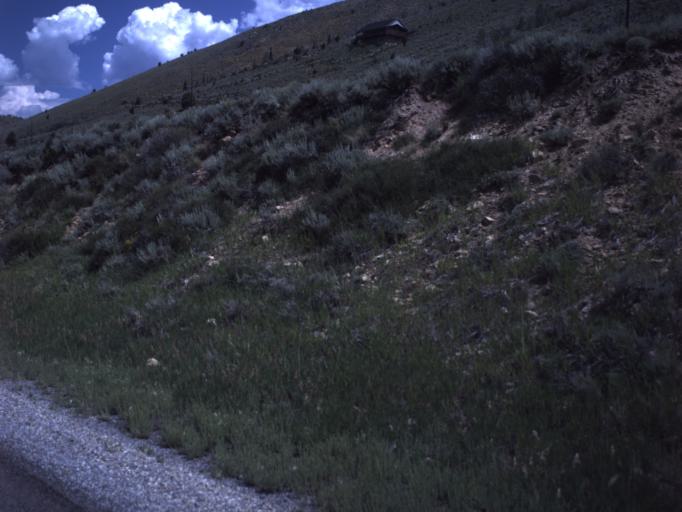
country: US
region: Utah
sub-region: Carbon County
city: Helper
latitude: 39.8067
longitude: -111.1349
